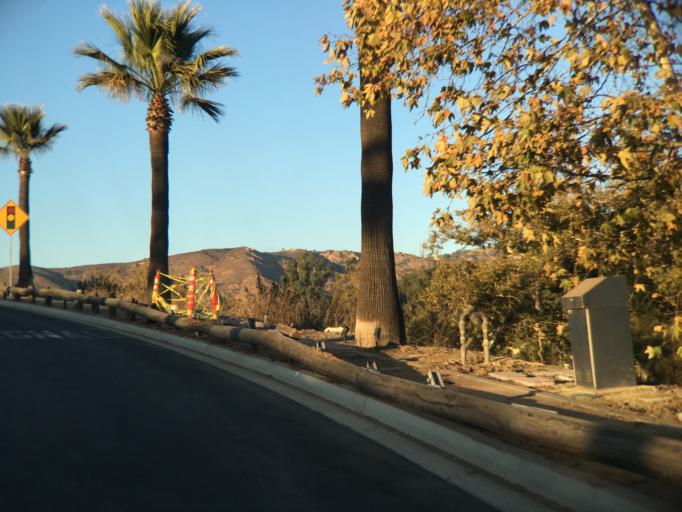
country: US
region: California
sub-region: San Diego County
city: Harbison Canyon
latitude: 32.7902
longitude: -116.8311
